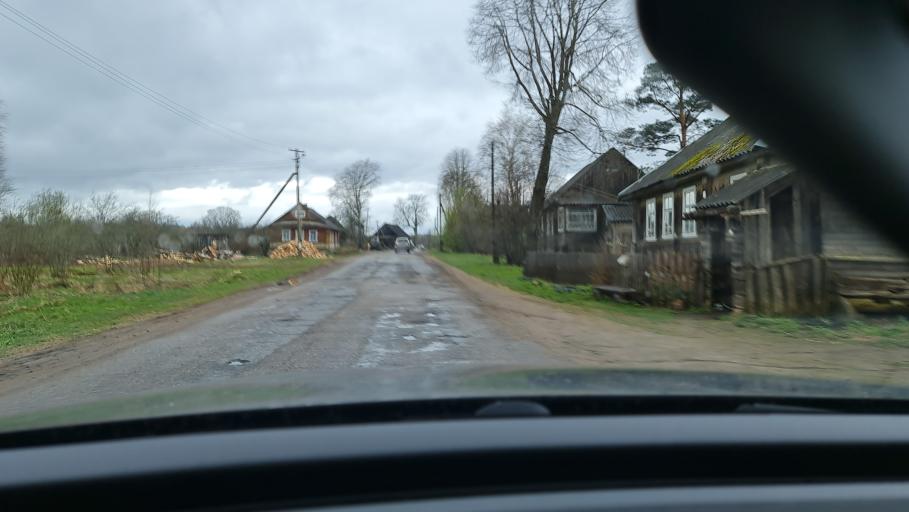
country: RU
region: Novgorod
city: Marevo
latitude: 57.2419
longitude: 32.0478
